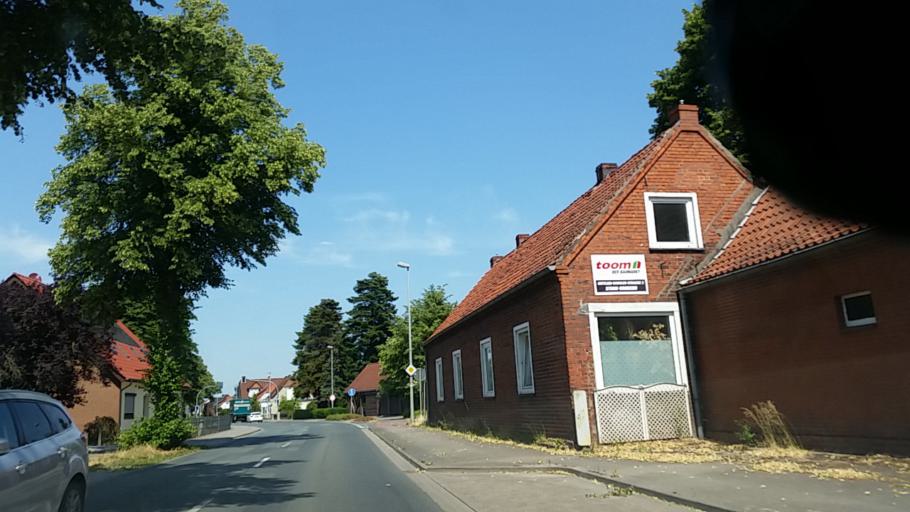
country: DE
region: Lower Saxony
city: Riede
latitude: 52.9787
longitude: 8.8757
